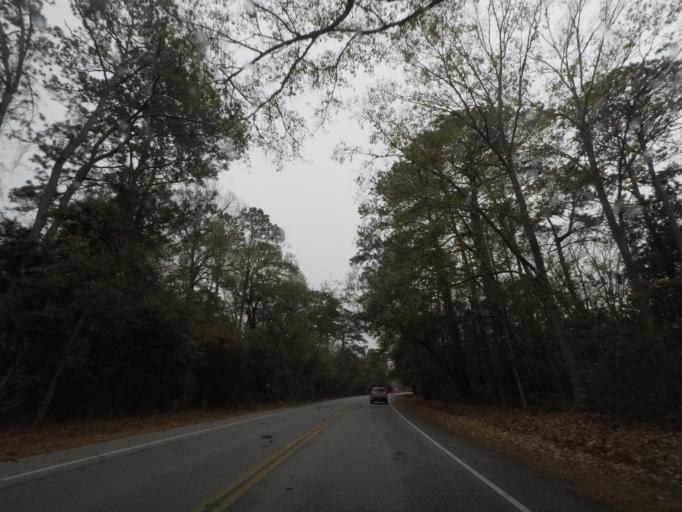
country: US
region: South Carolina
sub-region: Charleston County
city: Seabrook Island
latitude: 32.5493
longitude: -80.2805
